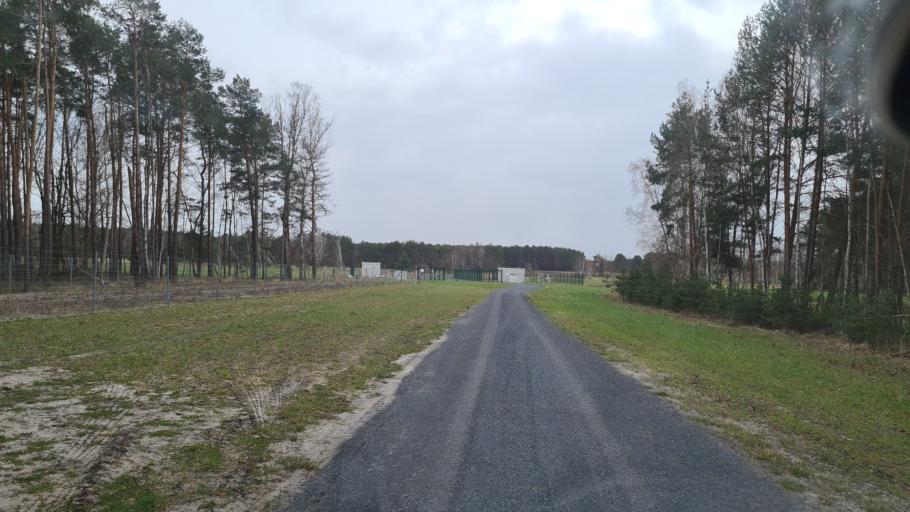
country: DE
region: Brandenburg
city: Finsterwalde
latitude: 51.5636
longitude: 13.6829
